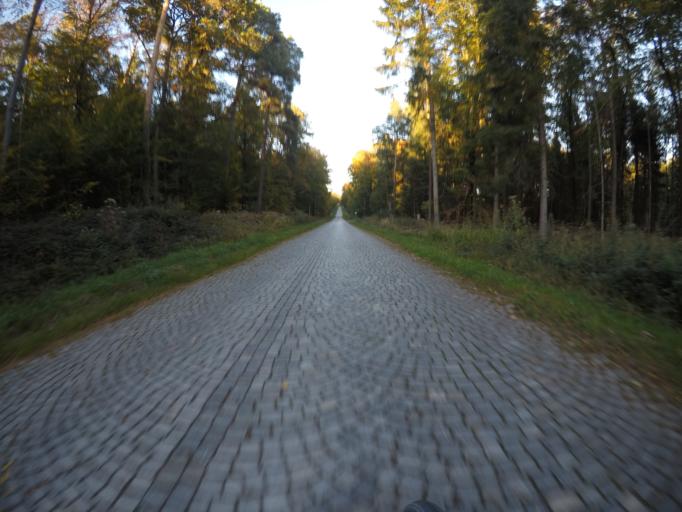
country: DE
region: Baden-Wuerttemberg
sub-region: Regierungsbezirk Stuttgart
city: Schonaich
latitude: 48.7099
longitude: 9.0796
